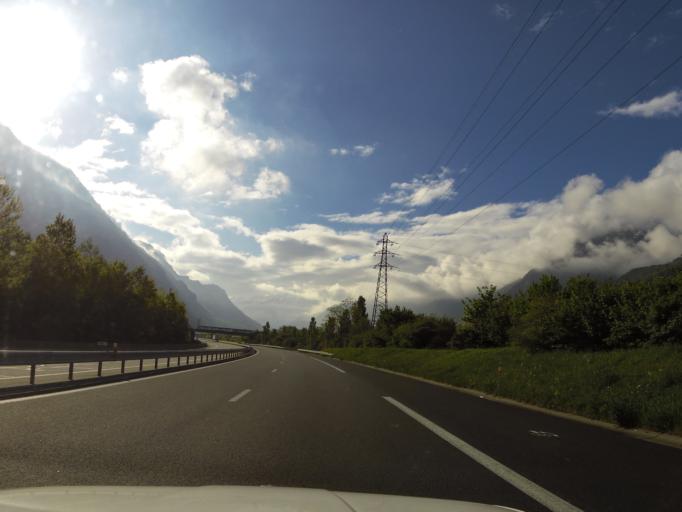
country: FR
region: Rhone-Alpes
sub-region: Departement de la Savoie
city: Saint-Jean-de-Maurienne
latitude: 45.2774
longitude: 6.3598
